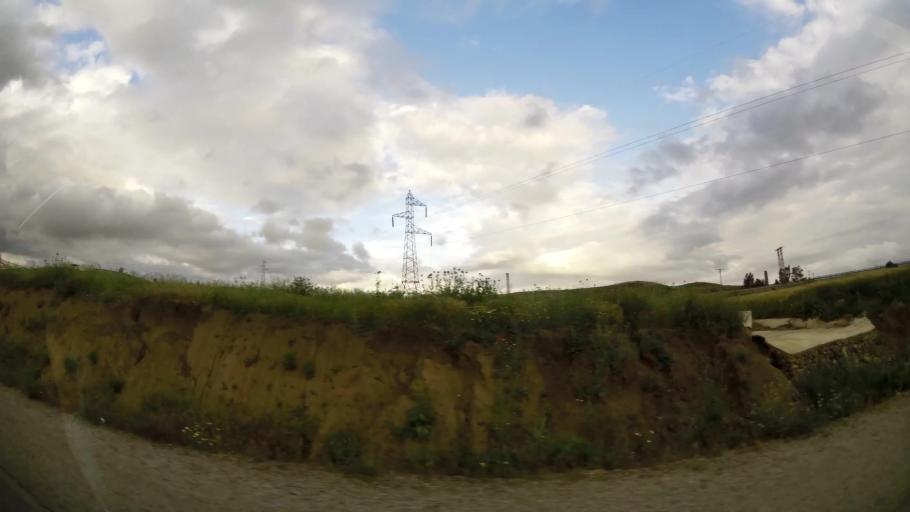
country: MA
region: Taza-Al Hoceima-Taounate
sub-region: Taza
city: Taza
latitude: 34.2616
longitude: -3.9594
